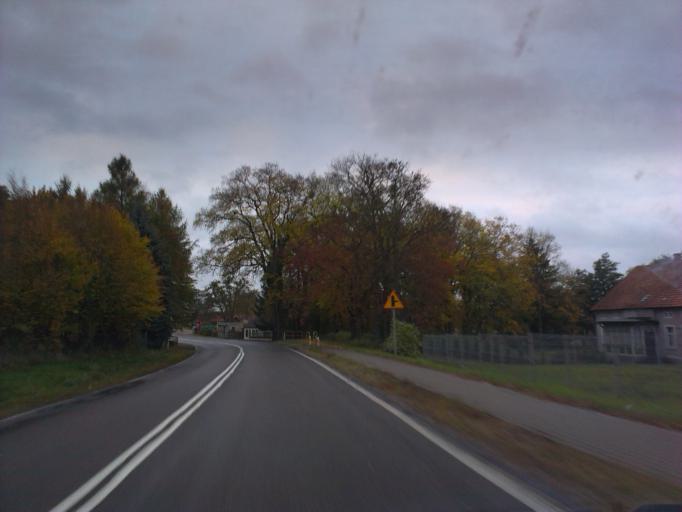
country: PL
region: Kujawsko-Pomorskie
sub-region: Powiat tucholski
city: Cekcyn
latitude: 53.5189
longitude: 17.9524
